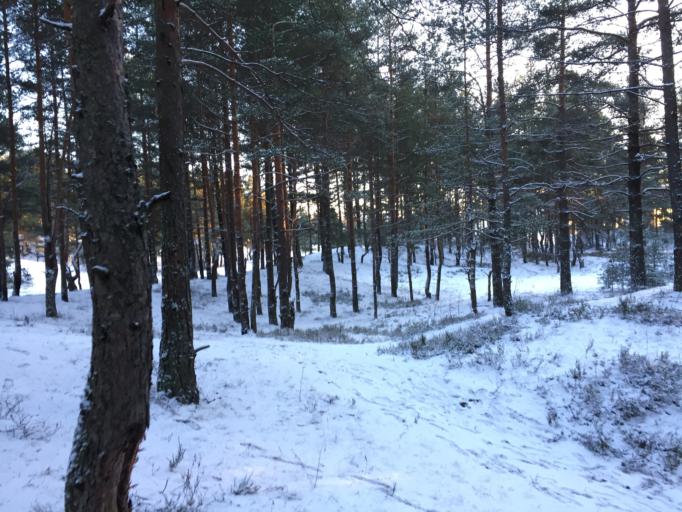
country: LV
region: Kekava
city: Balozi
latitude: 56.8798
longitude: 24.1170
